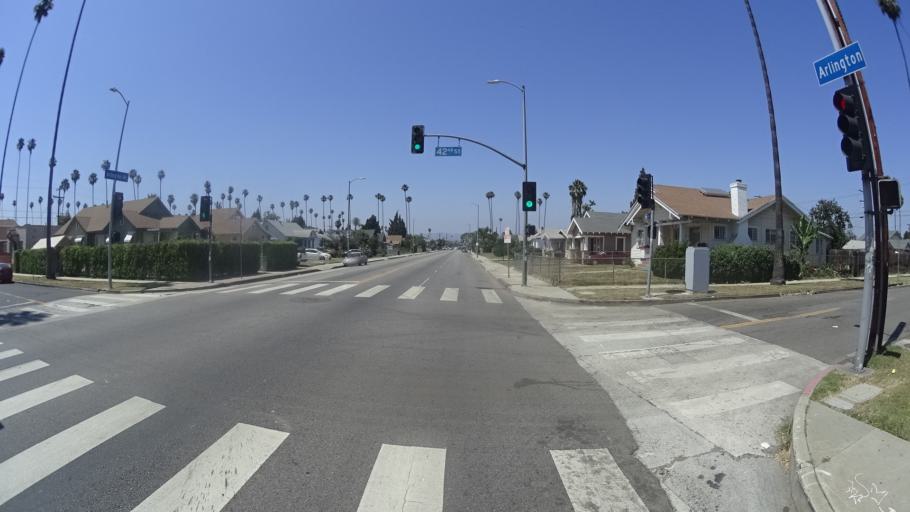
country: US
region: California
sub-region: Los Angeles County
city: View Park-Windsor Hills
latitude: 34.0071
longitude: -118.3182
